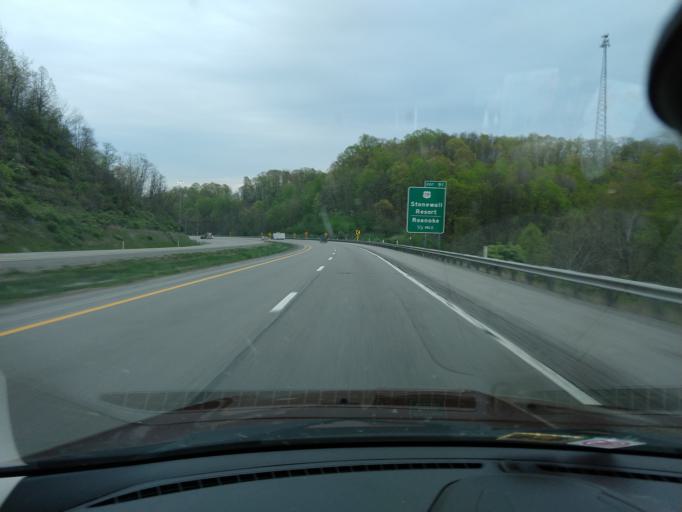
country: US
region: West Virginia
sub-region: Lewis County
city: Weston
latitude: 38.9604
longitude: -80.5221
